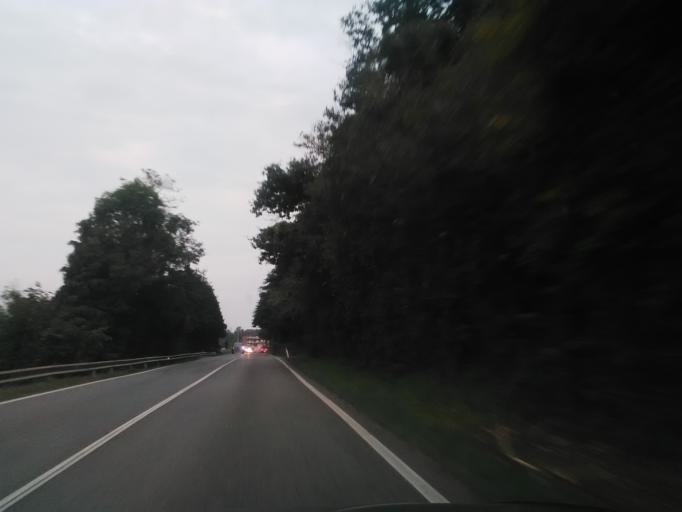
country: IT
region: Piedmont
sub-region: Provincia di Vercelli
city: Borgosesia
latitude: 45.7065
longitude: 8.2854
